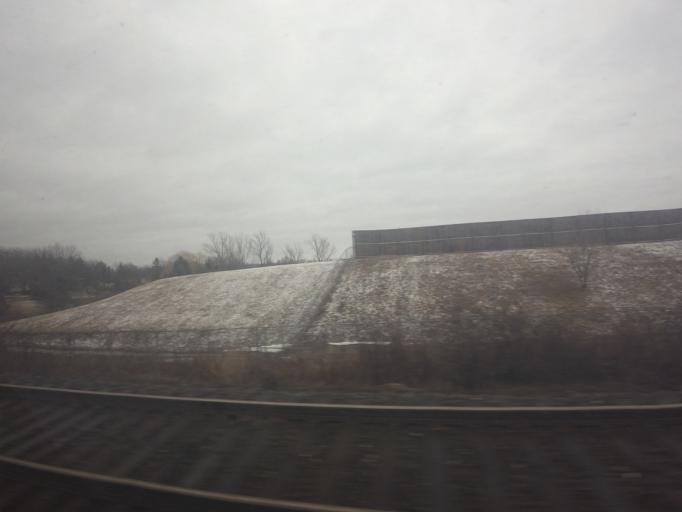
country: CA
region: Ontario
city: Kingston
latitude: 44.2289
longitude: -76.6346
